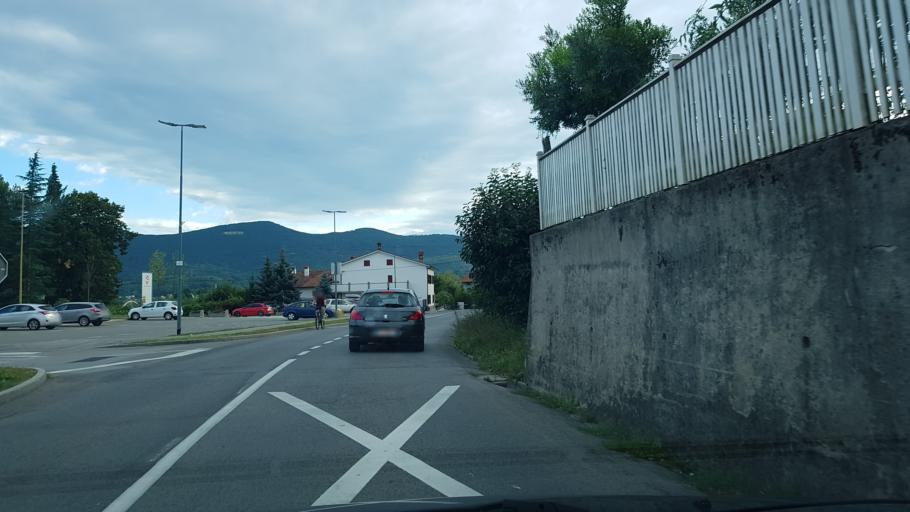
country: SI
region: Rence-Vogrsko
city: Rence
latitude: 45.8999
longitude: 13.6690
